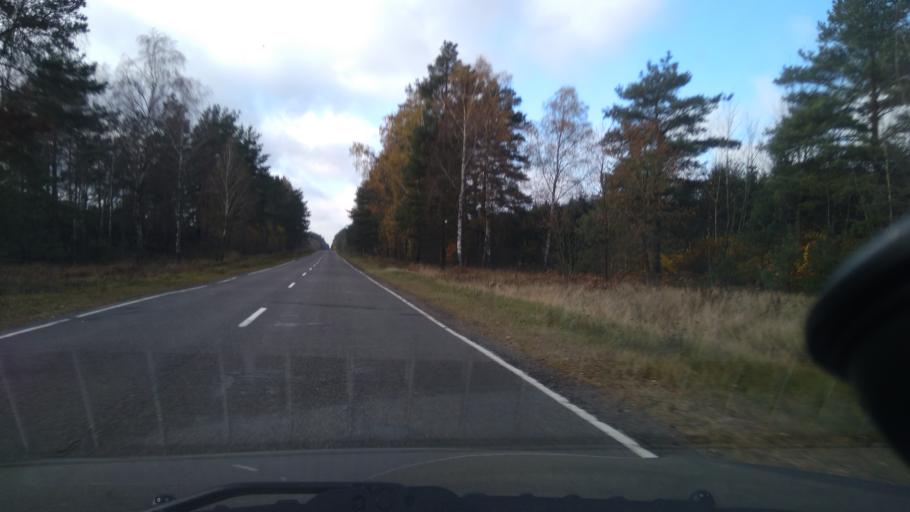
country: BY
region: Minsk
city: Slutsk
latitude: 53.2289
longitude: 27.7197
